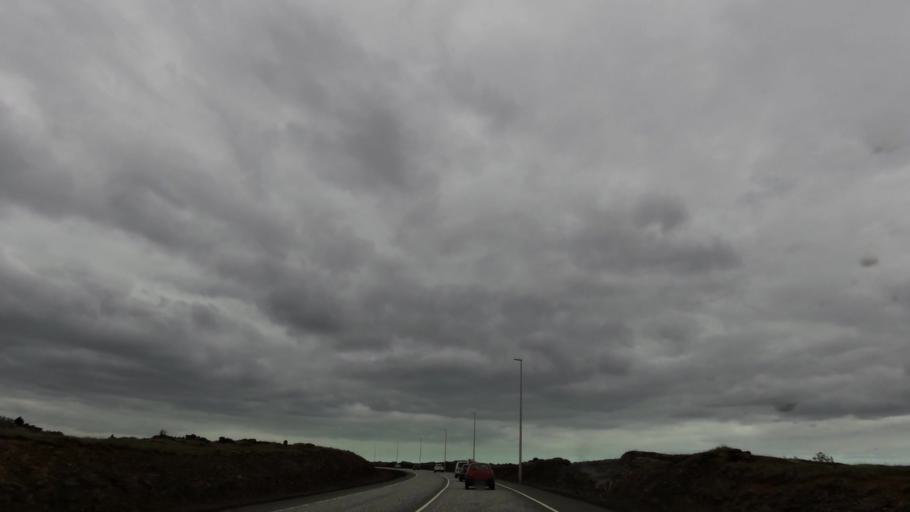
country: IS
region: Capital Region
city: Hafnarfjoerdur
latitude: 64.0898
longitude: -21.9650
